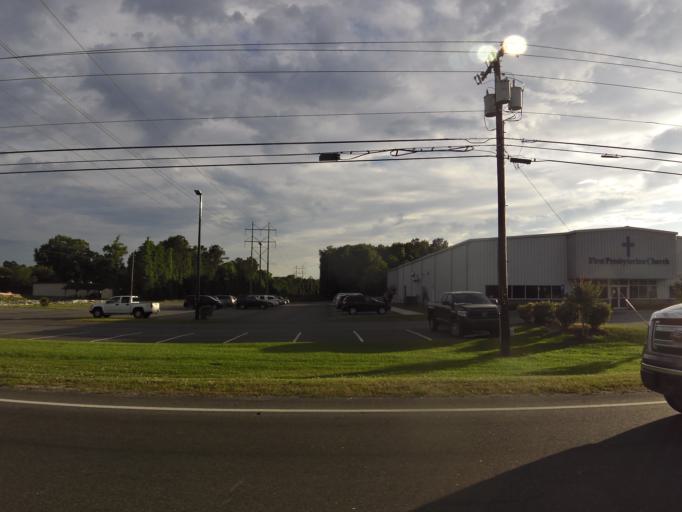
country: US
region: Georgia
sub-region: Chatham County
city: Pooler
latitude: 32.1057
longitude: -81.2278
